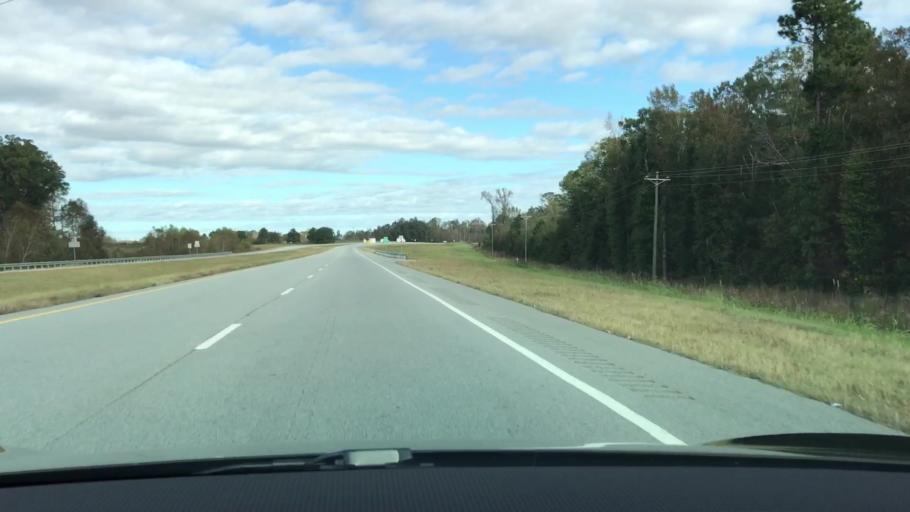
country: US
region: Georgia
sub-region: Jefferson County
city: Wadley
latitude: 32.8128
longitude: -82.4035
